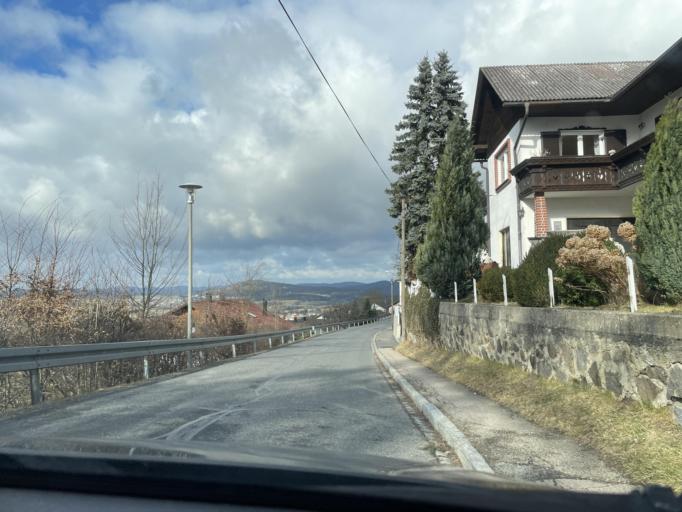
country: DE
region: Bavaria
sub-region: Upper Palatinate
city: Runding
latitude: 49.2162
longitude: 12.7617
